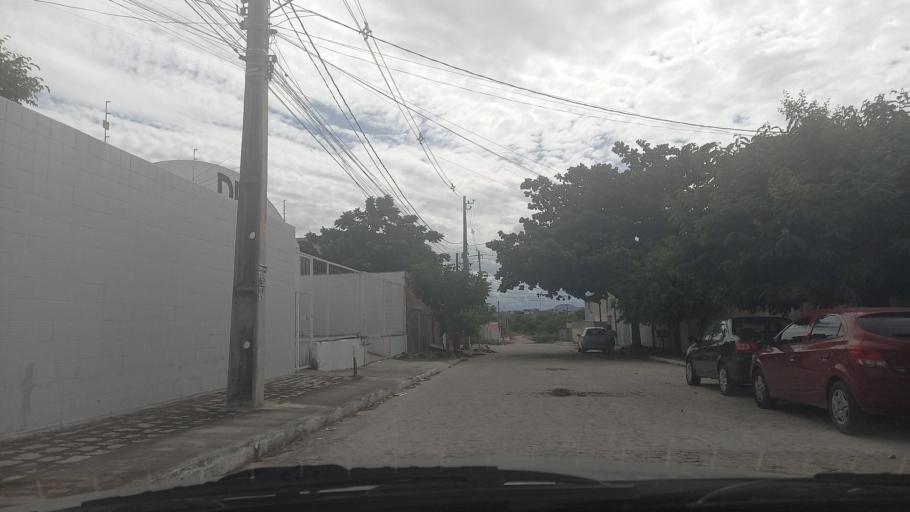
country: BR
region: Pernambuco
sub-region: Caruaru
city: Caruaru
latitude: -8.2917
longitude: -35.9876
